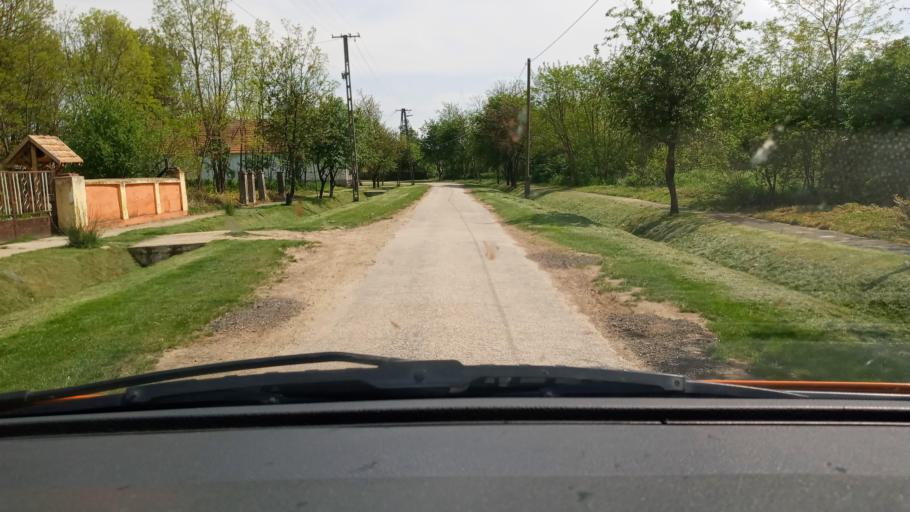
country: HR
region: Osjecko-Baranjska
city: Beli Manastir
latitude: 45.7967
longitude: 18.5262
